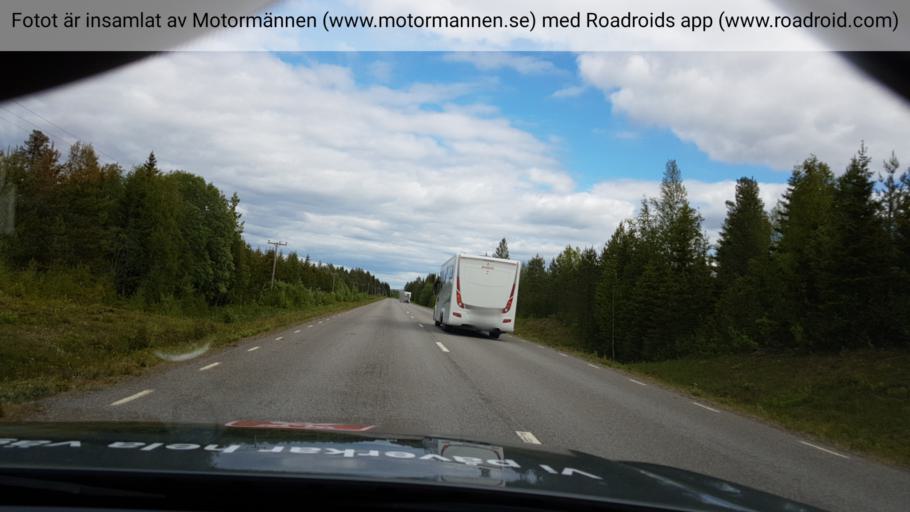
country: SE
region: Jaemtland
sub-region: Stroemsunds Kommun
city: Stroemsund
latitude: 64.2337
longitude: 15.4689
